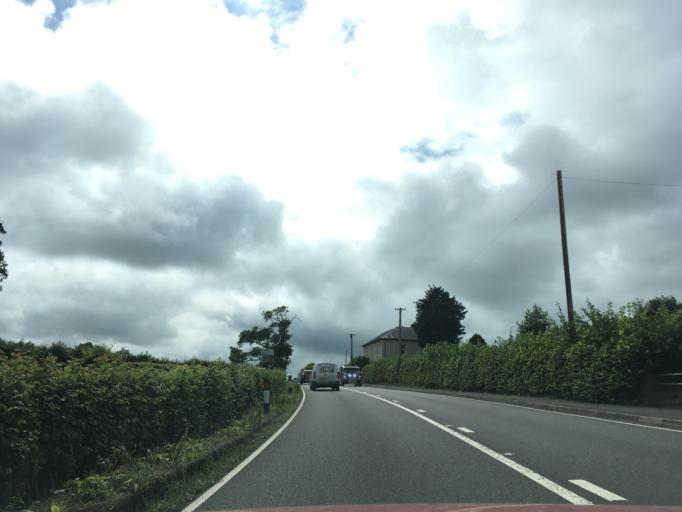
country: GB
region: Wales
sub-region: Carmarthenshire
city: Llangathen
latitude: 51.8854
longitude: -4.0643
